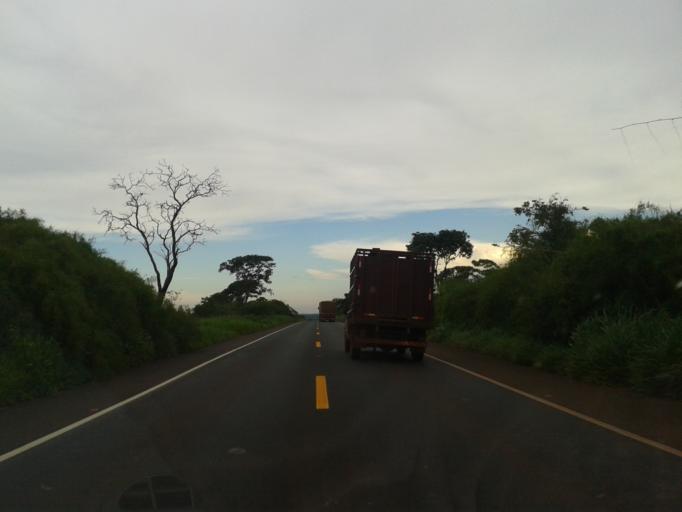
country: BR
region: Minas Gerais
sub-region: Santa Vitoria
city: Santa Vitoria
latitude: -18.8845
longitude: -50.1455
